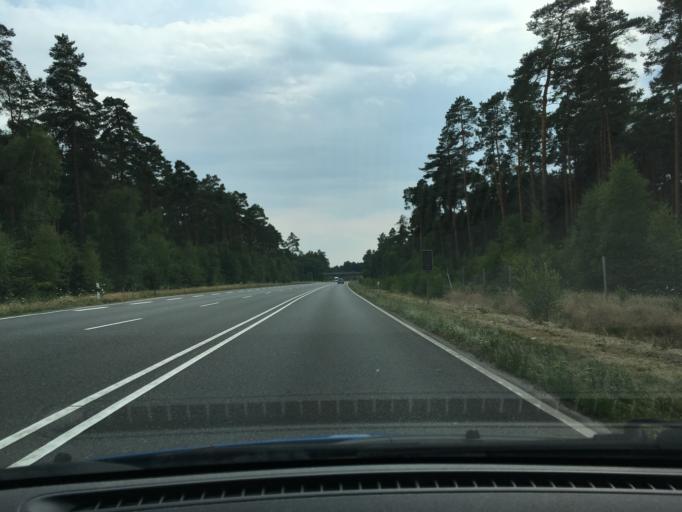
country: DE
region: Lower Saxony
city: Adelheidsdorf
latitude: 52.5645
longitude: 10.0752
